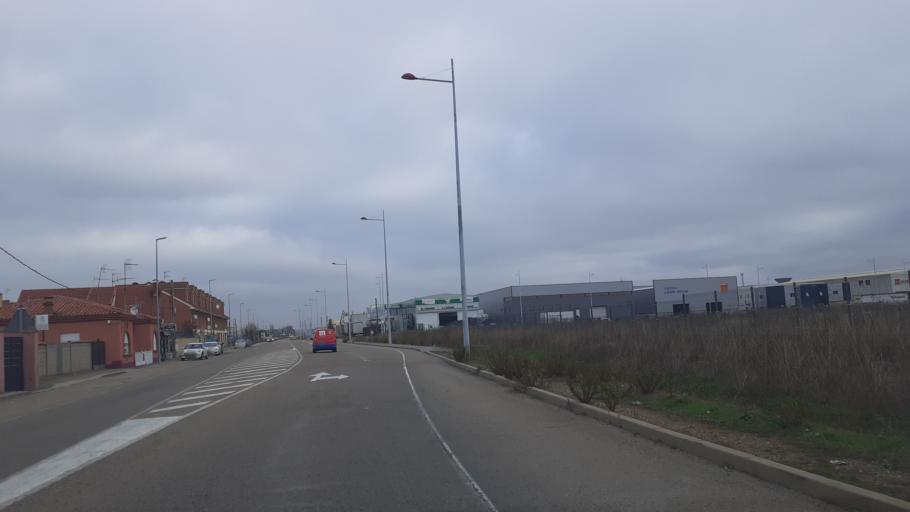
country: ES
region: Castille and Leon
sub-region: Provincia de Leon
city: Onzonilla
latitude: 42.5388
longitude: -5.5903
